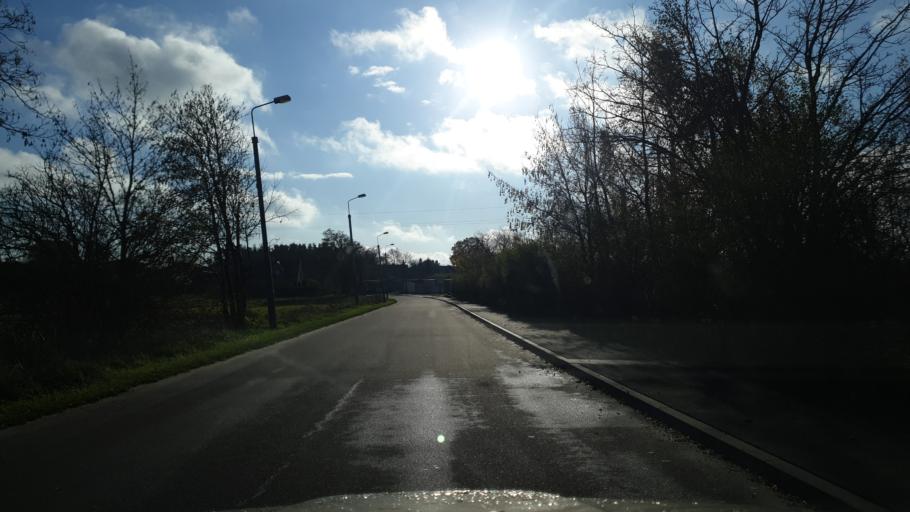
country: PL
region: Pomeranian Voivodeship
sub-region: Powiat pucki
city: Jastrzebia Gora
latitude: 54.8271
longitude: 18.2440
